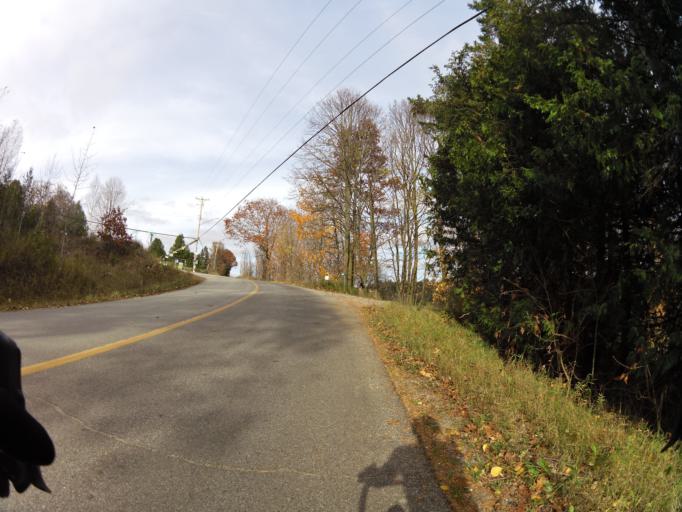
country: CA
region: Quebec
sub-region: Outaouais
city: Wakefield
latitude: 45.7327
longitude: -75.9732
